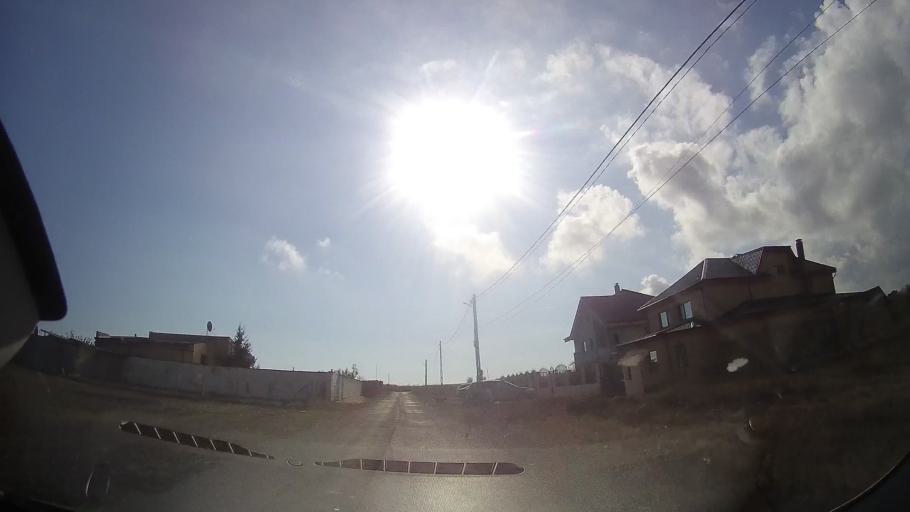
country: RO
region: Constanta
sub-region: Comuna Tuzla
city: Tuzla
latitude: 43.9965
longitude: 28.6443
